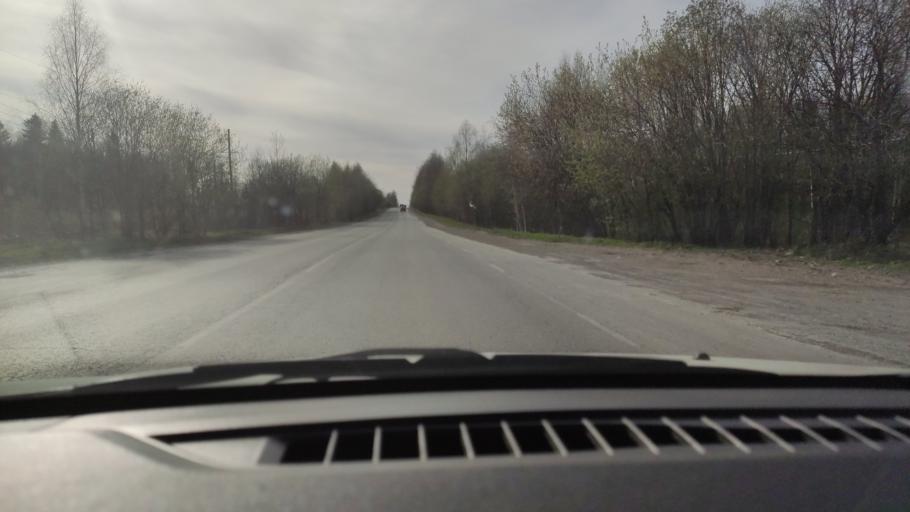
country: RU
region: Perm
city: Ferma
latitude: 57.9403
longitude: 56.4458
